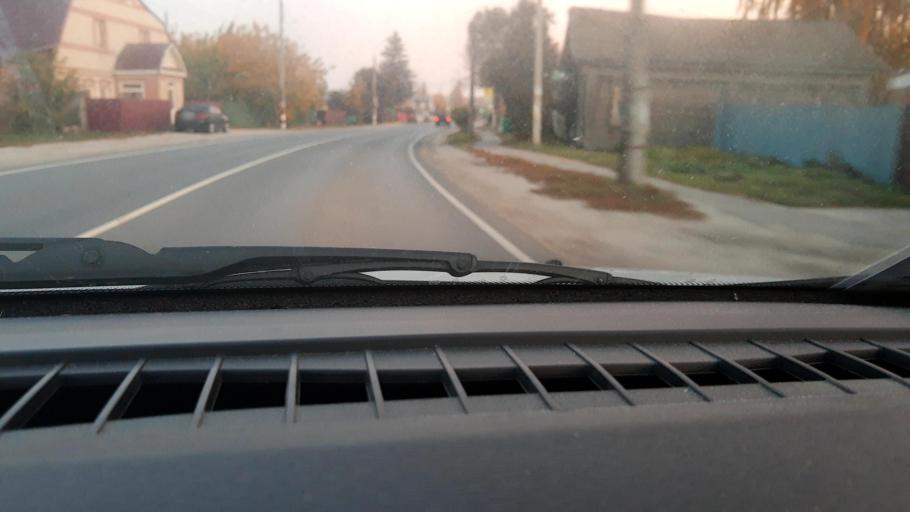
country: RU
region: Nizjnij Novgorod
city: Neklyudovo
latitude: 56.3801
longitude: 44.0153
